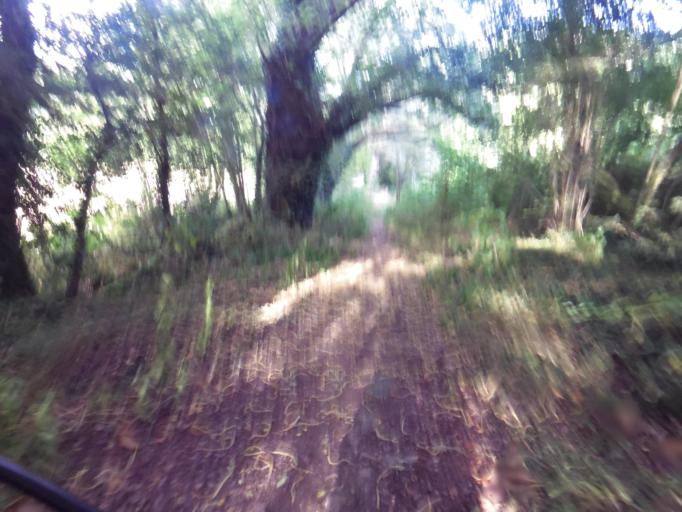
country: FR
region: Brittany
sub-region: Departement du Morbihan
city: Pluherlin
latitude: 47.7017
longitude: -2.4022
